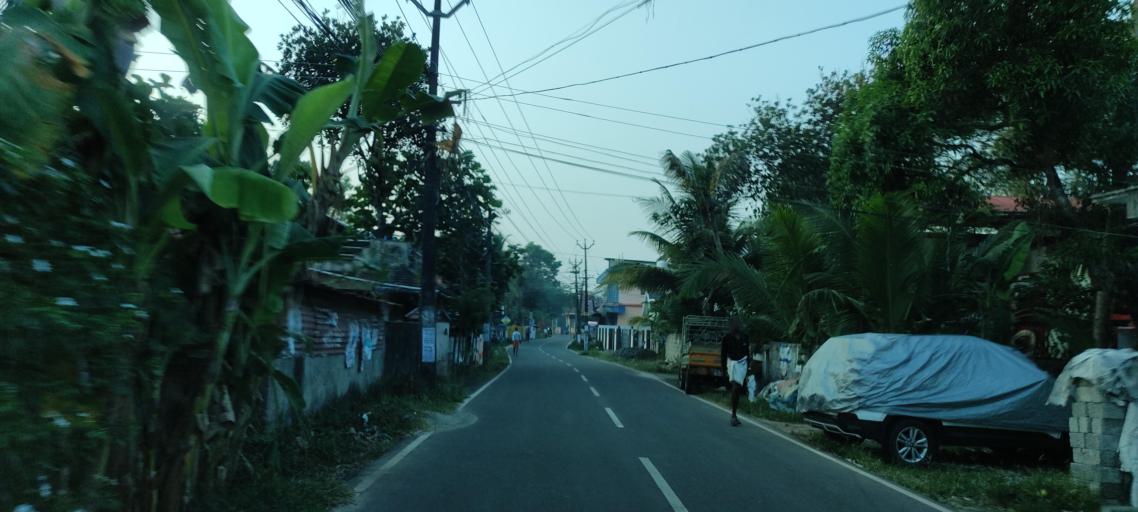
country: IN
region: Kerala
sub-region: Alappuzha
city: Alleppey
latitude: 9.4400
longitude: 76.3469
